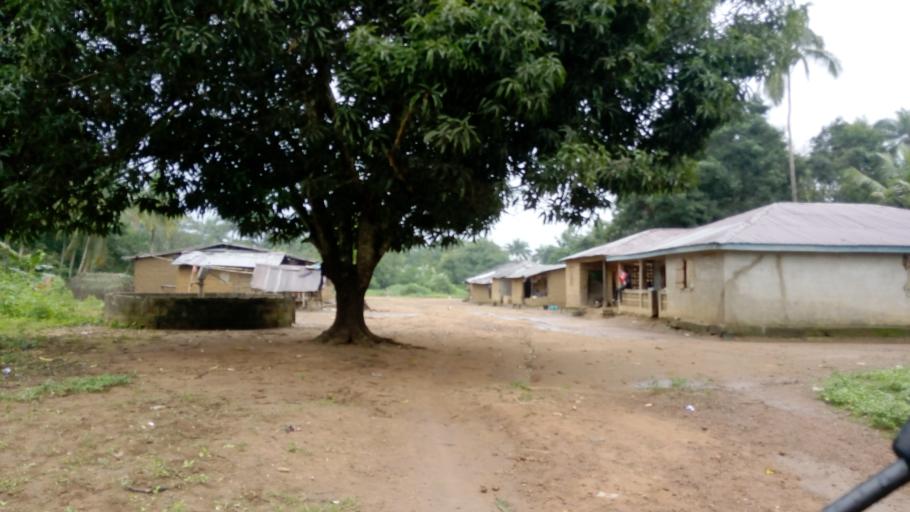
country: SL
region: Northern Province
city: Port Loko
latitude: 8.5006
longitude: -12.7509
